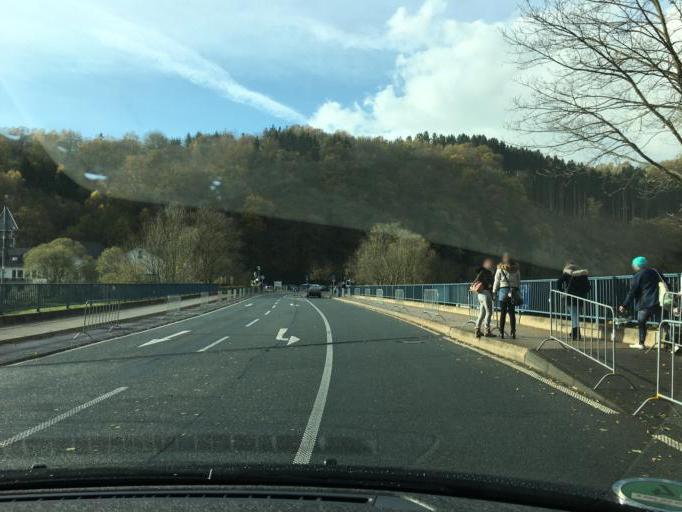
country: DE
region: North Rhine-Westphalia
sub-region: Regierungsbezirk Koln
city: Simmerath
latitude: 50.5812
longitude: 6.3792
